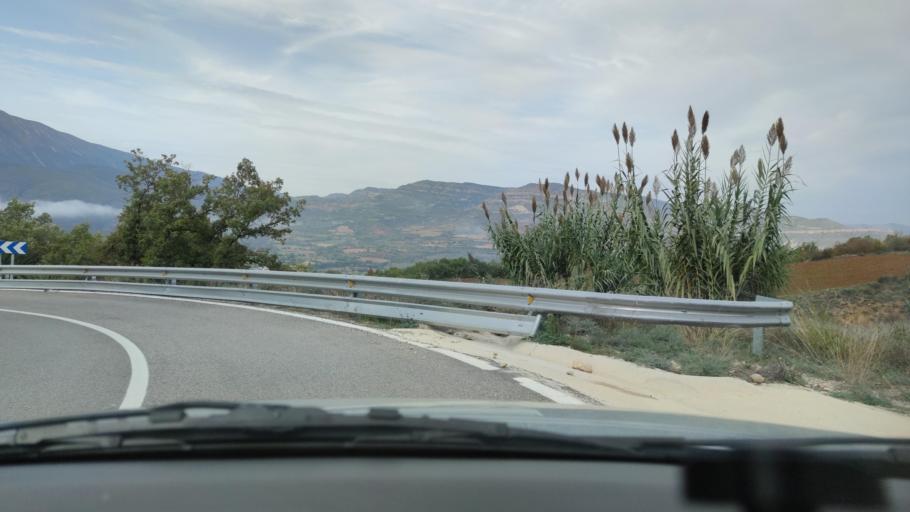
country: ES
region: Catalonia
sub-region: Provincia de Lleida
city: Llimiana
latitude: 42.0678
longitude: 0.9120
